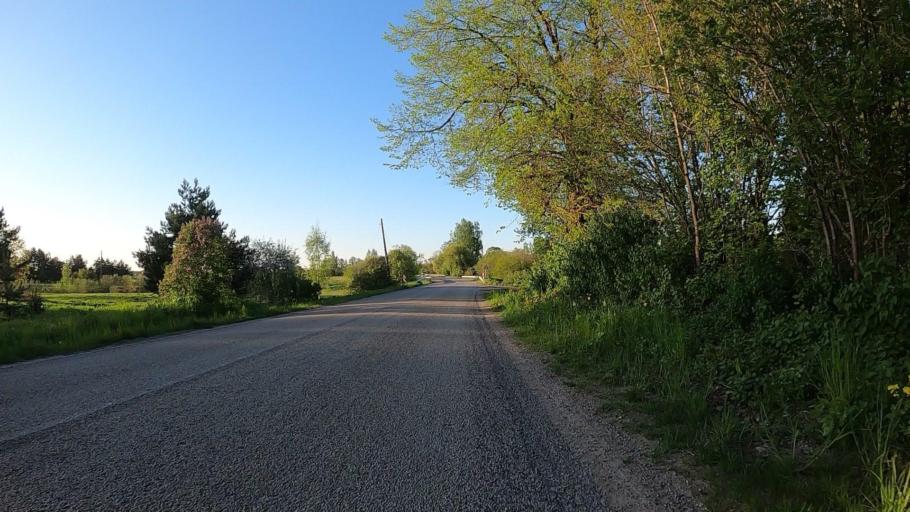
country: LV
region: Kekava
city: Kekava
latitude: 56.8118
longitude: 24.2028
